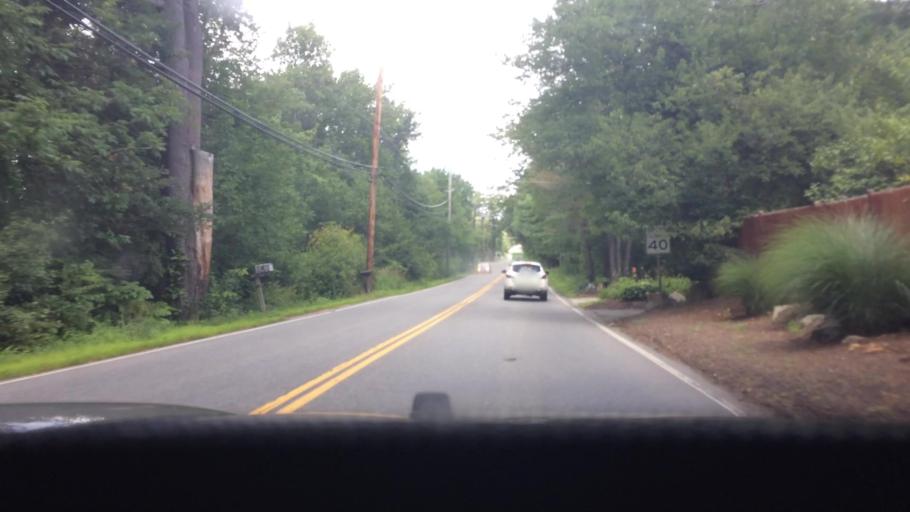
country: US
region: Massachusetts
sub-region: Middlesex County
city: Maynard
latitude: 42.4466
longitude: -71.4539
